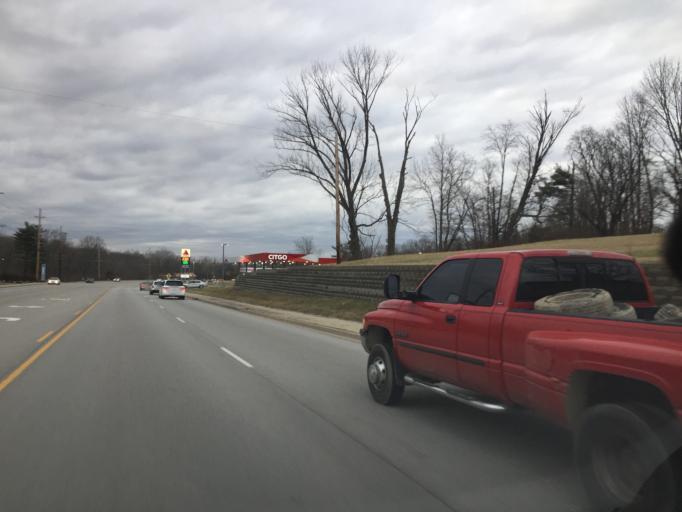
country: US
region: Indiana
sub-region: Monroe County
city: Ellettsville
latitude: 39.2123
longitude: -86.5874
